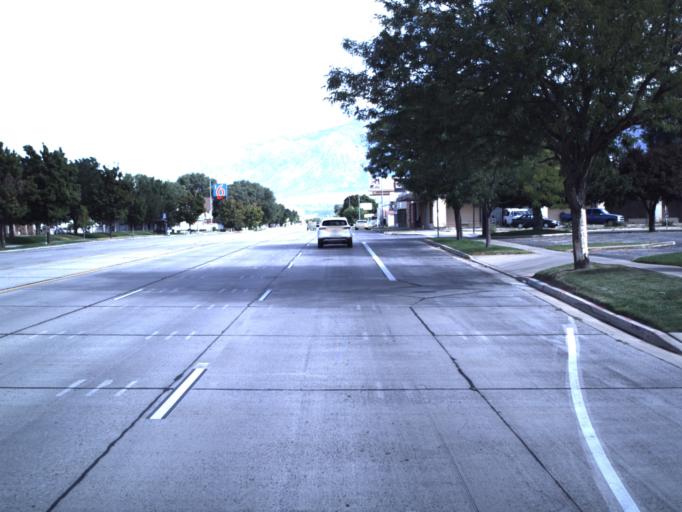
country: US
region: Utah
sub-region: Weber County
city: Ogden
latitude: 41.2381
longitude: -111.9700
